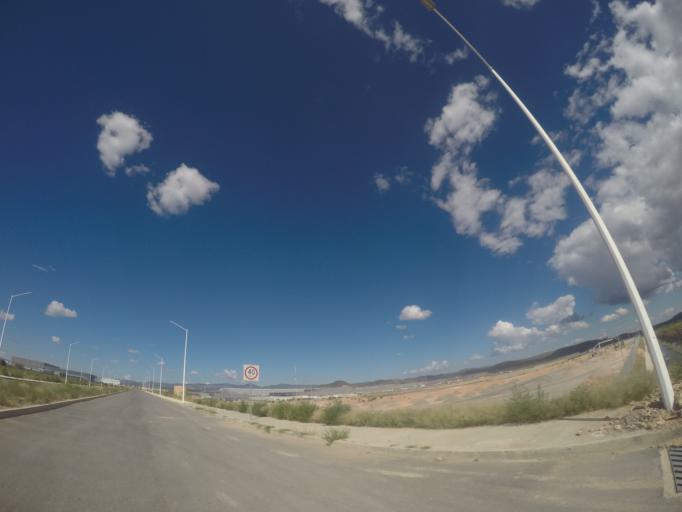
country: MX
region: San Luis Potosi
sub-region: Zaragoza
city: Cerro Gordo
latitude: 21.9675
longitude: -100.8615
